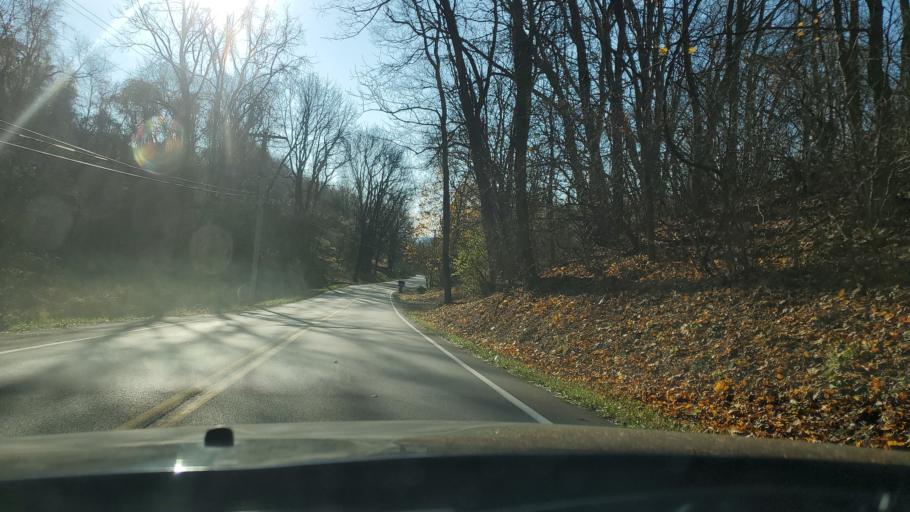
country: US
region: Pennsylvania
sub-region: Cumberland County
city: Mechanicsburg
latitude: 40.1710
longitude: -76.9872
